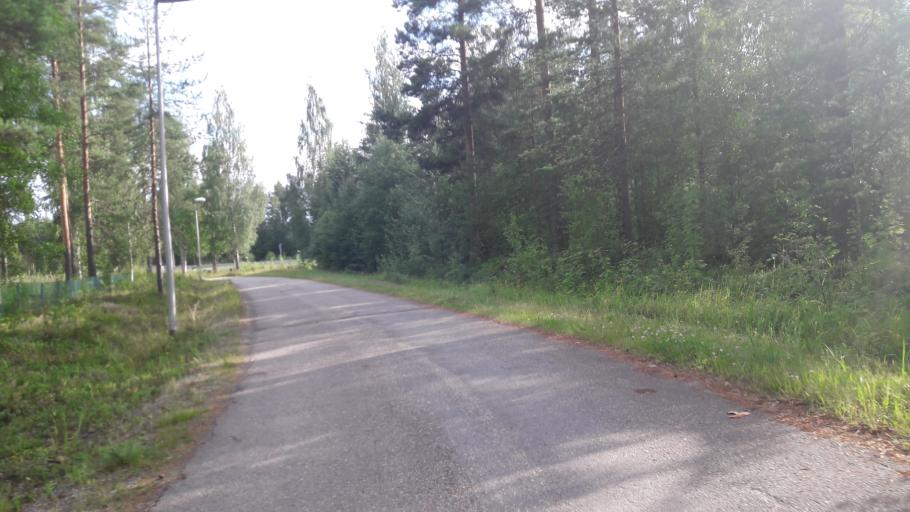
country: FI
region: North Karelia
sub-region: Joensuu
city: Joensuu
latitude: 62.6192
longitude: 29.7300
